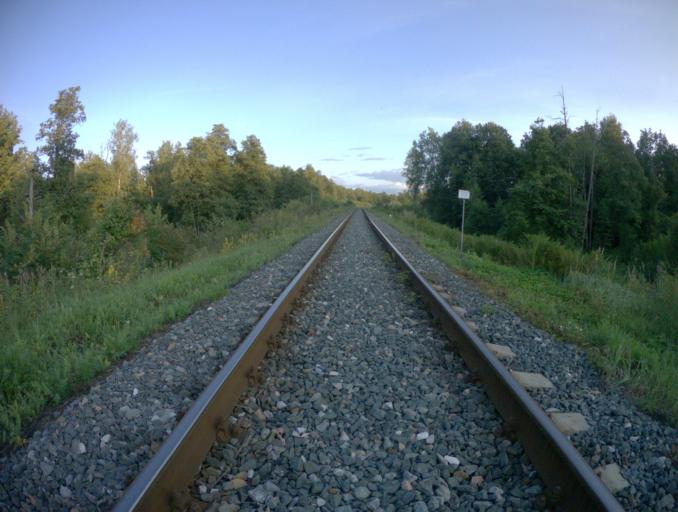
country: RU
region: Vladimir
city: Raduzhnyy
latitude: 56.0427
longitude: 40.3844
